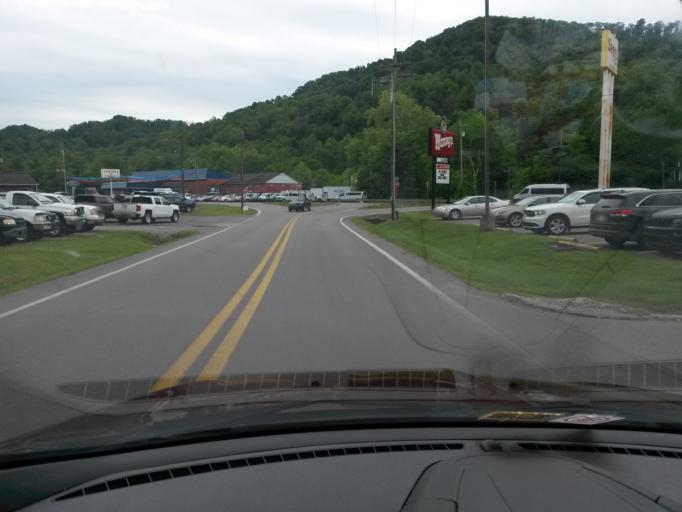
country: US
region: West Virginia
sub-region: Lewis County
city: Weston
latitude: 39.0364
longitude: -80.4472
